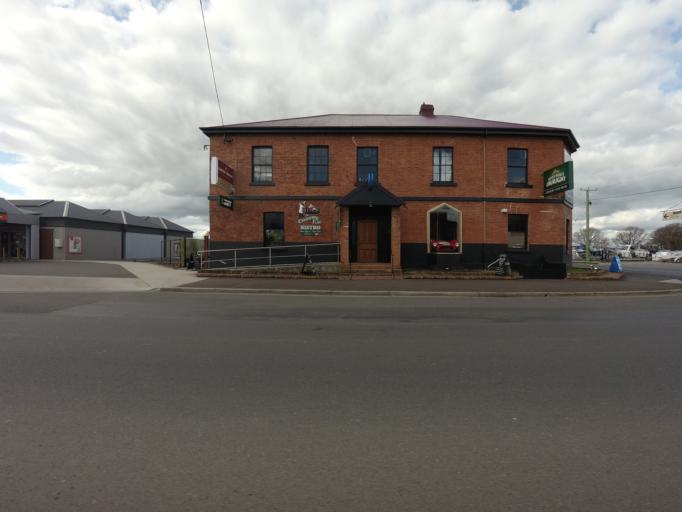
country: AU
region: Tasmania
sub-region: Northern Midlands
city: Longford
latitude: -41.5890
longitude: 147.1201
